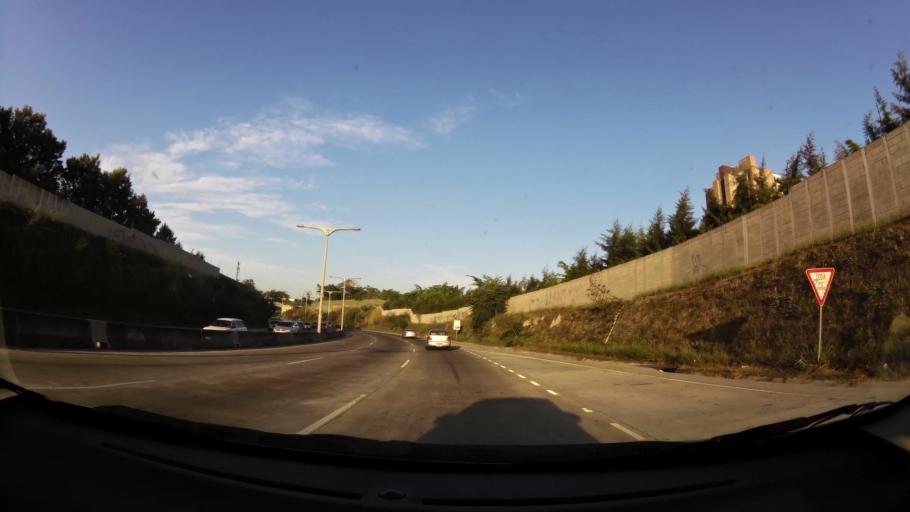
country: SV
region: La Libertad
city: Antiguo Cuscatlan
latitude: 13.6845
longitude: -89.2438
